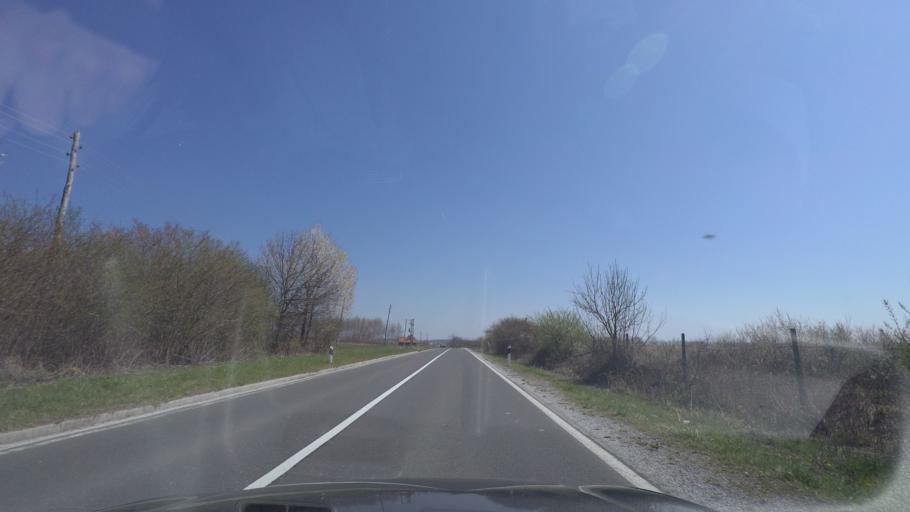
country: HR
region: Sisacko-Moslavacka
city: Gvozd
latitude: 45.3318
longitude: 15.9229
